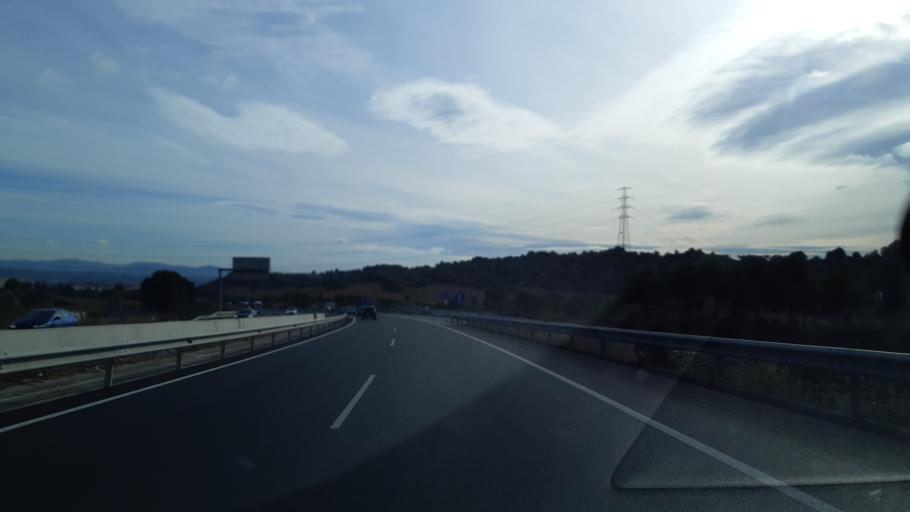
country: ES
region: Catalonia
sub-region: Provincia de Barcelona
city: Collbato
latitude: 41.5570
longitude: 1.8356
